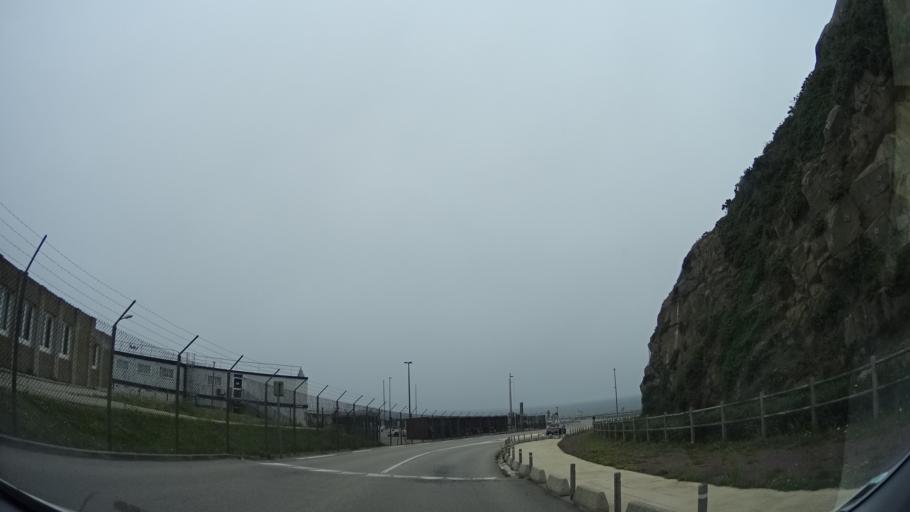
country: FR
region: Lower Normandy
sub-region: Departement de la Manche
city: Flamanville
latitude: 49.5439
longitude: -1.8740
